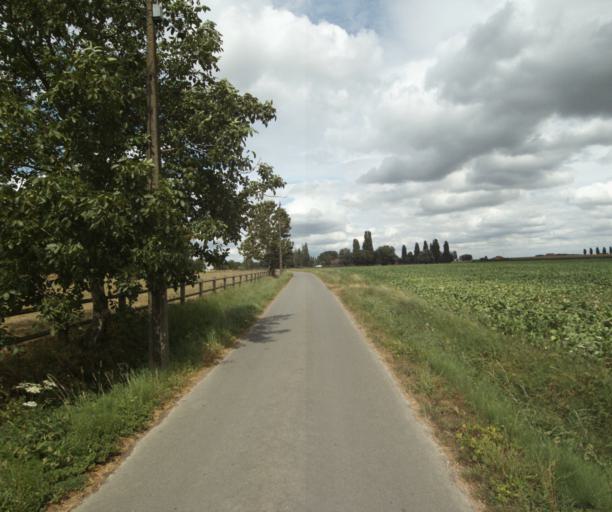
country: FR
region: Nord-Pas-de-Calais
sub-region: Departement du Nord
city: Linselles
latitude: 50.7497
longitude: 3.0649
